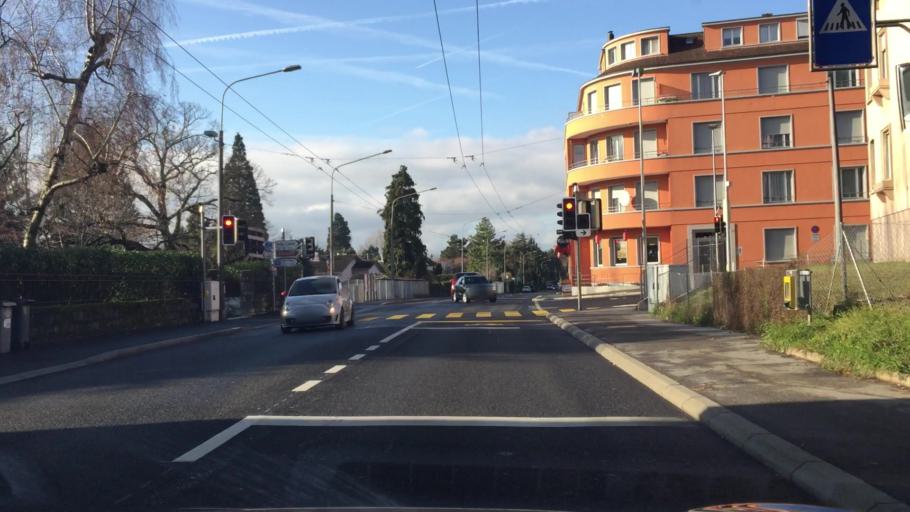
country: CH
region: Vaud
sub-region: Lavaux-Oron District
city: Pully
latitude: 46.5066
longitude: 6.6543
